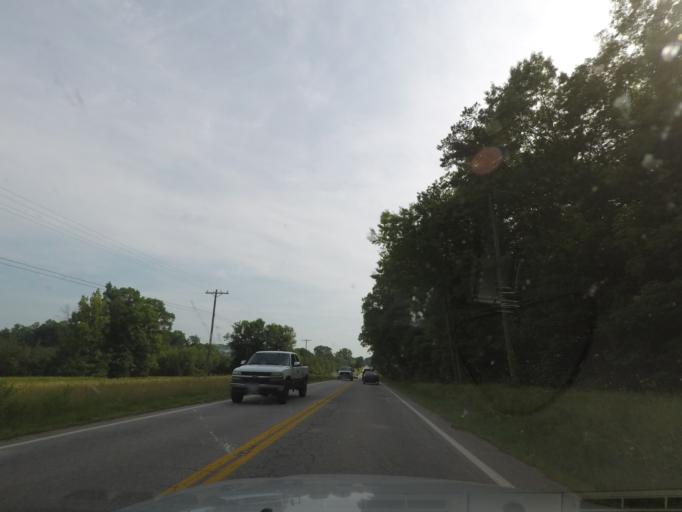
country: US
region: Virginia
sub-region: Prince Edward County
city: Hampden Sydney
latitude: 37.1804
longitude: -78.4332
